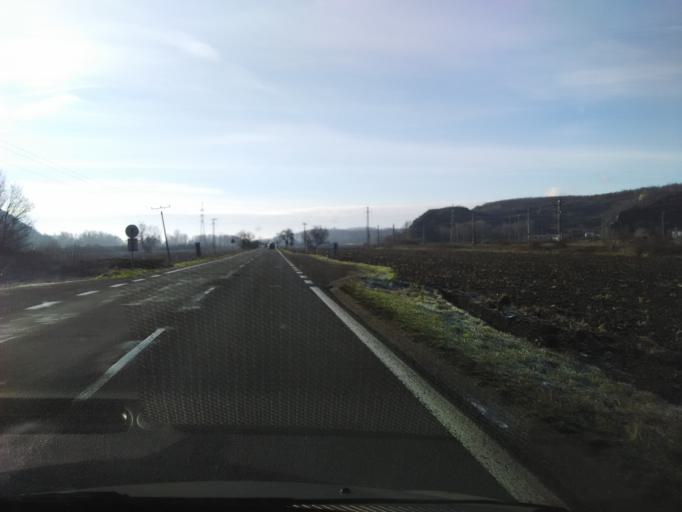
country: SK
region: Nitriansky
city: Tlmace
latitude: 48.3093
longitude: 18.5365
